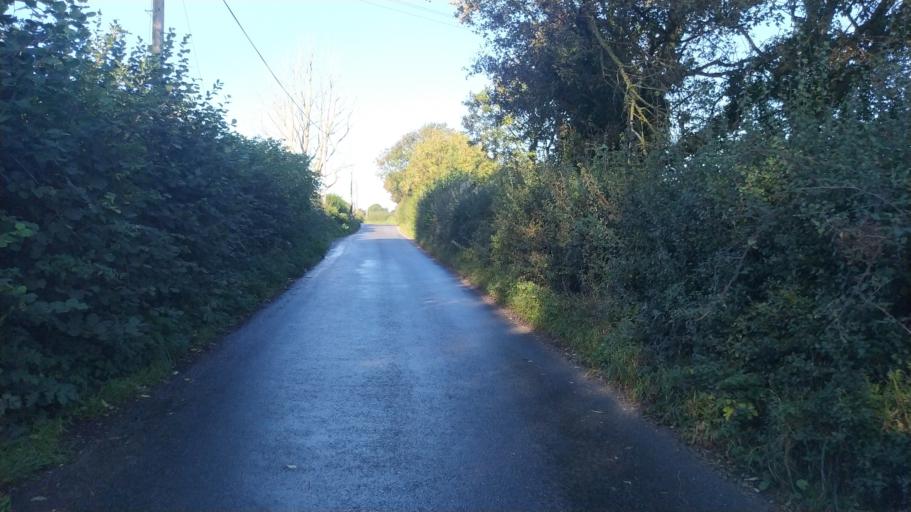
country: GB
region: England
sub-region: Dorset
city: Blandford Forum
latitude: 50.7755
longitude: -2.1752
